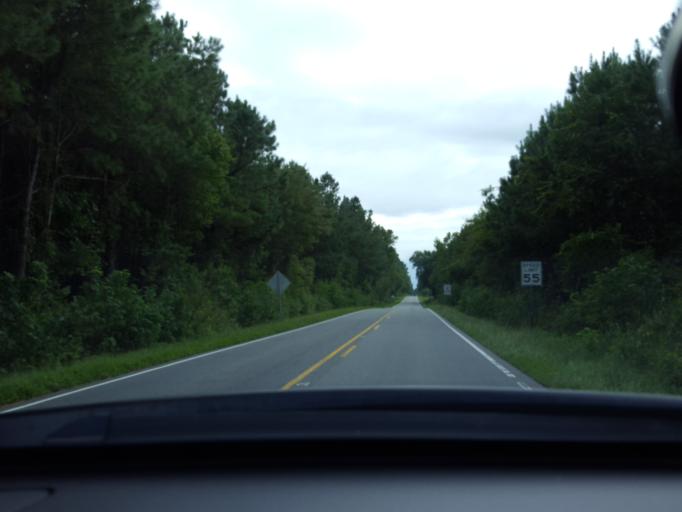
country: US
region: North Carolina
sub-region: Duplin County
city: Rose Hill
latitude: 34.8932
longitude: -78.0652
